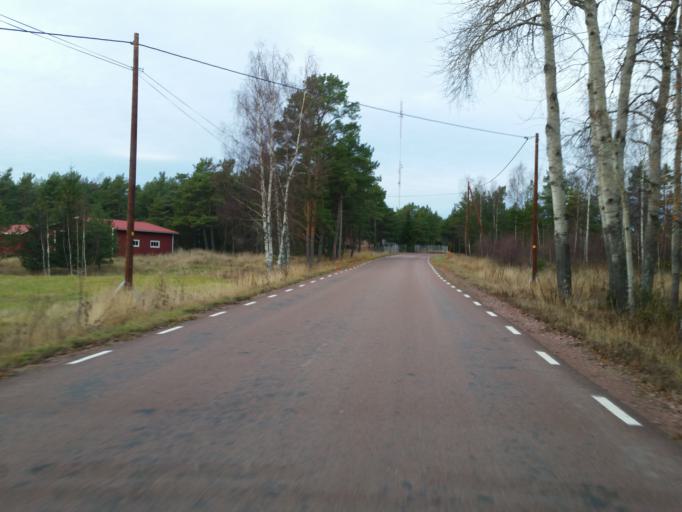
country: AX
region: Alands skaergard
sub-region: Kumlinge
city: Kumlinge
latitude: 60.2735
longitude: 20.7941
